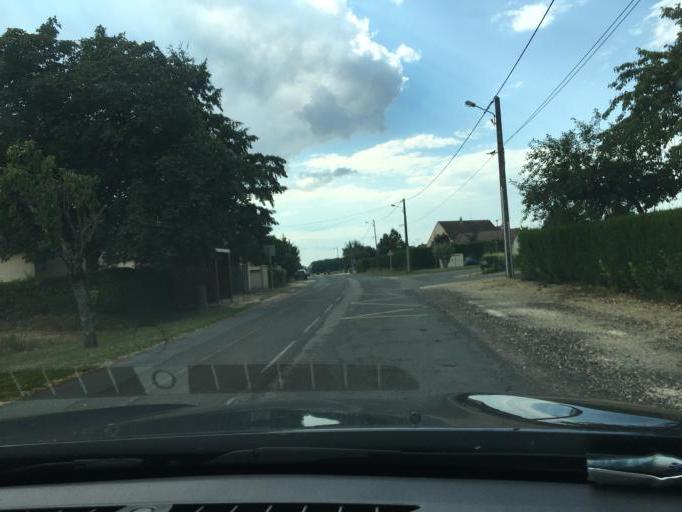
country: FR
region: Centre
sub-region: Departement du Cher
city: Baugy
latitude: 47.0990
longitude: 2.6703
